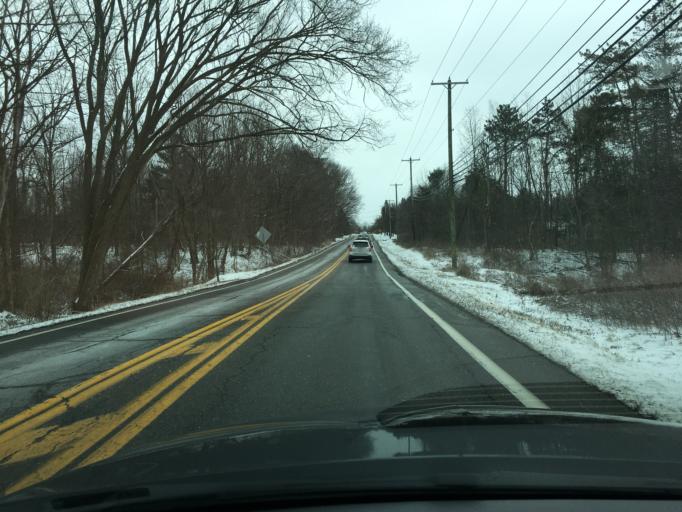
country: US
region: Ohio
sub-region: Summit County
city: Fairlawn
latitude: 41.1394
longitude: -81.5960
